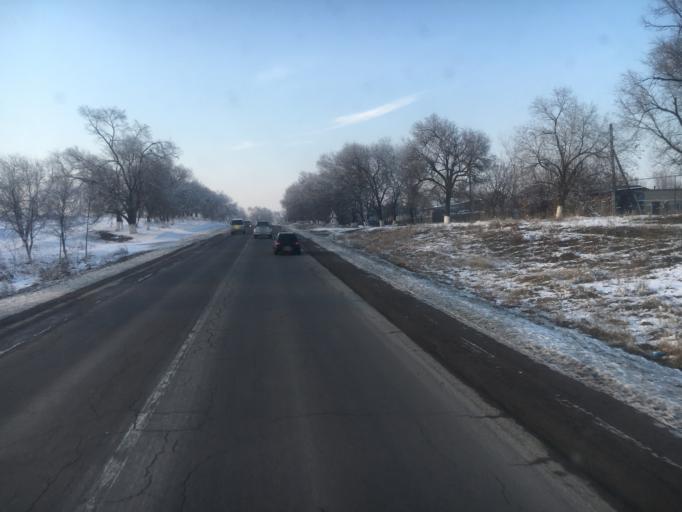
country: KZ
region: Almaty Oblysy
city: Burunday
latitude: 43.3059
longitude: 76.6694
